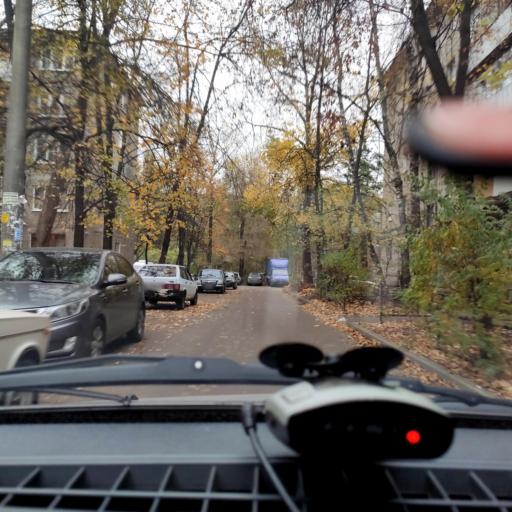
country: RU
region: Voronezj
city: Pridonskoy
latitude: 51.6487
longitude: 39.1235
